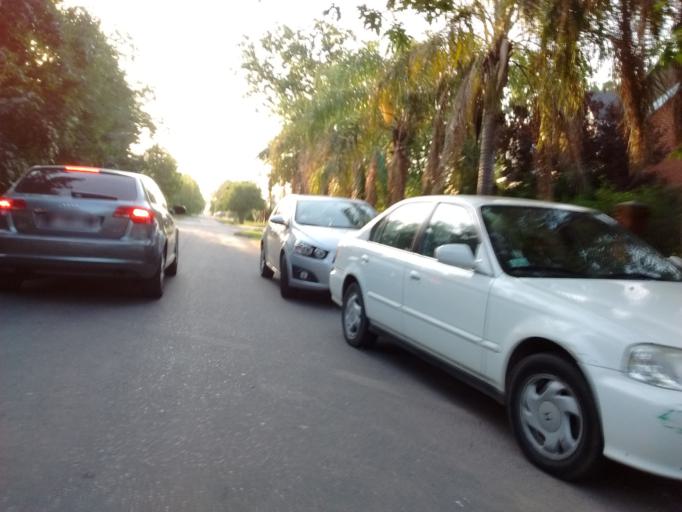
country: AR
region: Santa Fe
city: Funes
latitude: -32.9161
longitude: -60.7551
